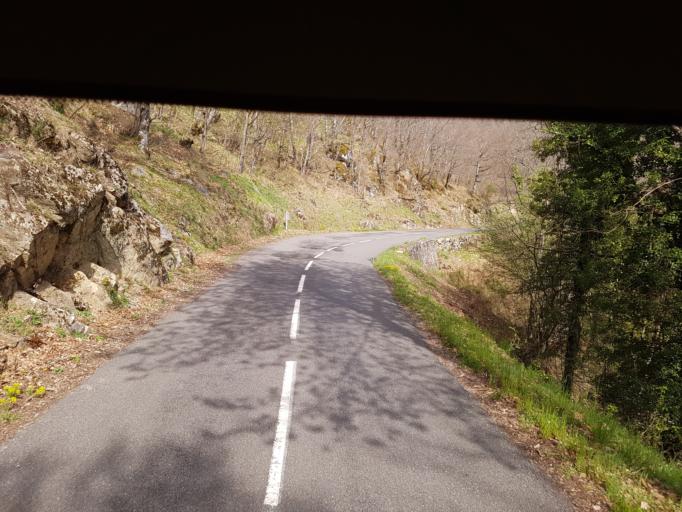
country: FR
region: Languedoc-Roussillon
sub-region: Departement de la Lozere
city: Florac
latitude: 44.3671
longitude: 3.7016
